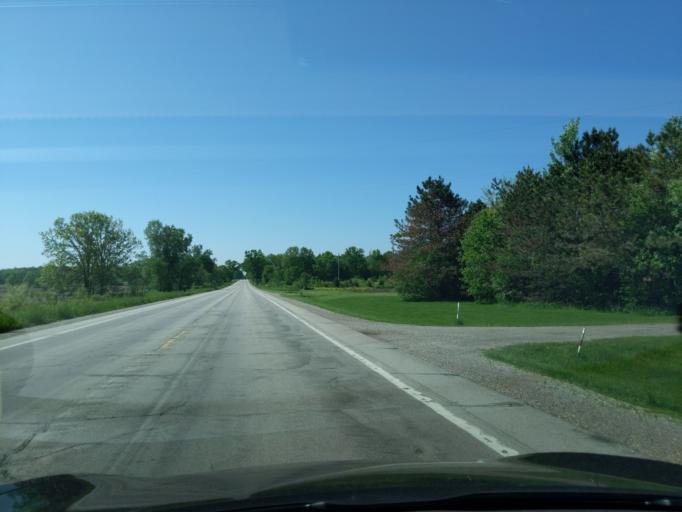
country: US
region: Michigan
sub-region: Ingham County
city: Stockbridge
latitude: 42.4951
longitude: -84.1902
